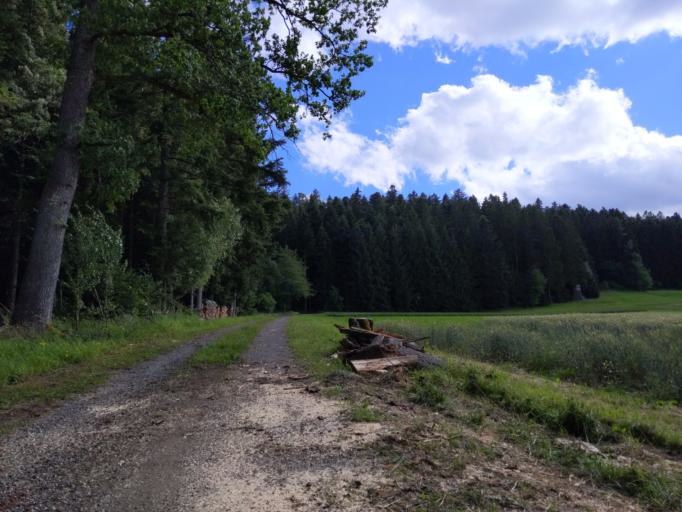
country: DE
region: Baden-Wuerttemberg
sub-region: Karlsruhe Region
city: Glatten
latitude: 48.4002
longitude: 8.5054
